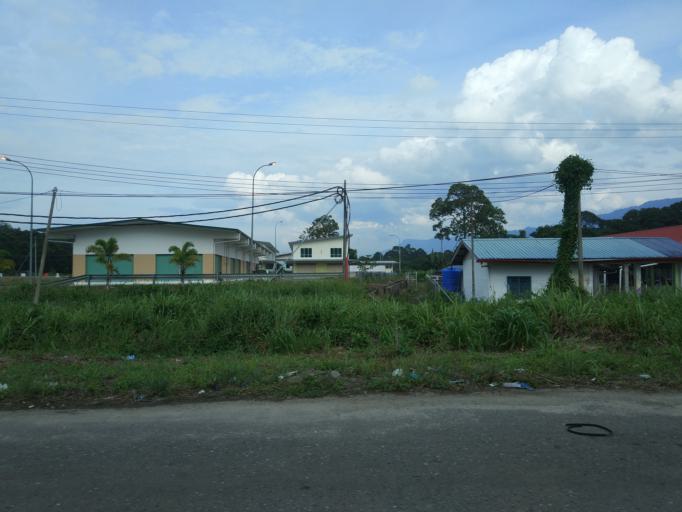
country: MY
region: Sabah
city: Bandar Labuan
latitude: 4.9620
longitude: 115.5061
